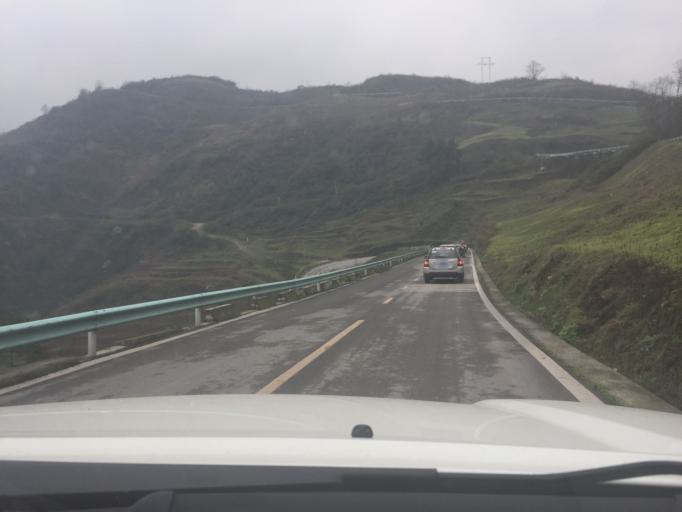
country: CN
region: Guizhou Sheng
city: Supu
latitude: 27.1016
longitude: 106.8152
